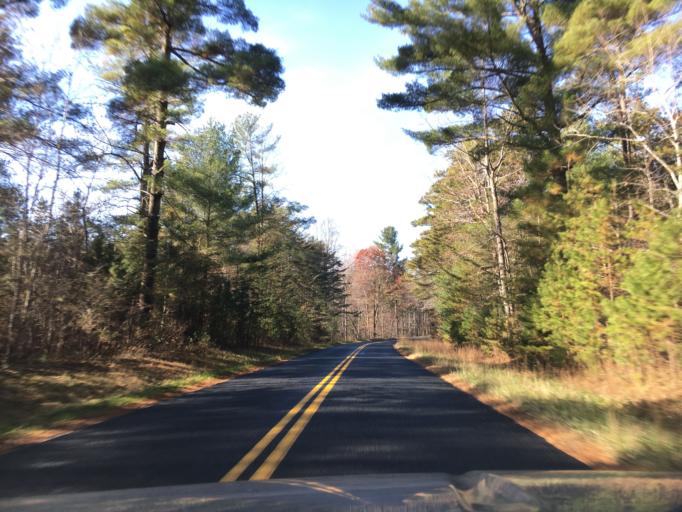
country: US
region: Virginia
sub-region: Buckingham County
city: Buckingham
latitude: 37.4366
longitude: -78.6613
